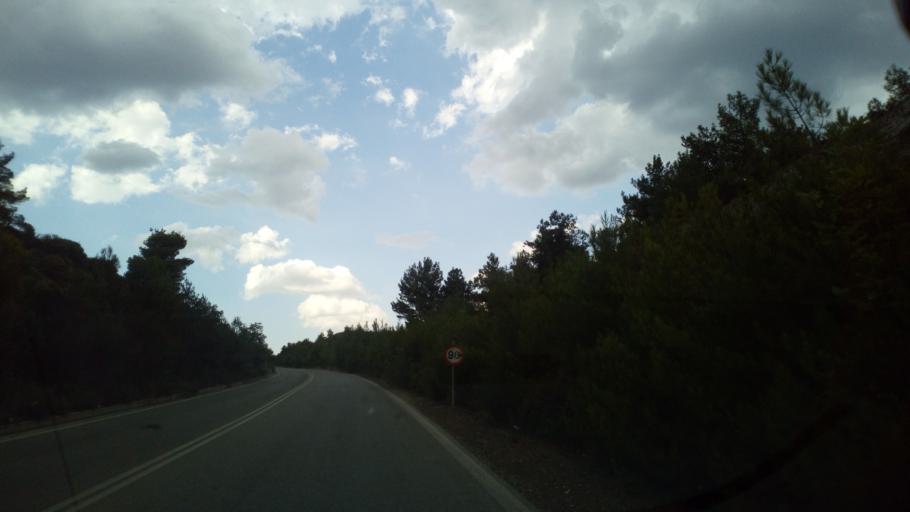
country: GR
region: Central Macedonia
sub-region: Nomos Chalkidikis
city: Polygyros
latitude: 40.3511
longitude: 23.4467
